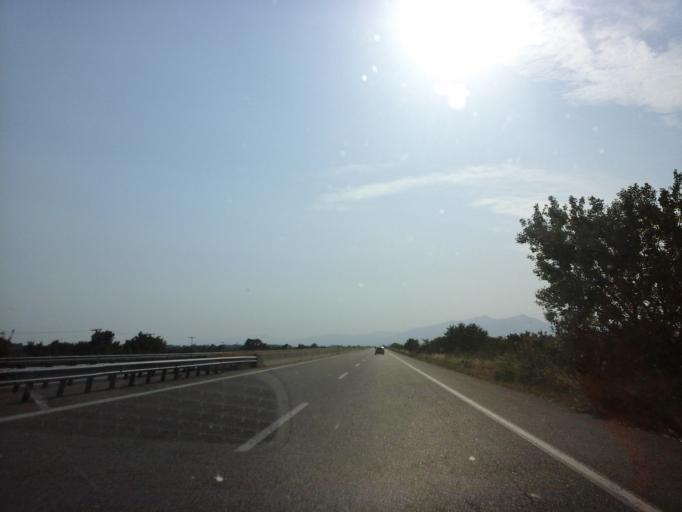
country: GR
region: East Macedonia and Thrace
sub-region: Nomos Xanthis
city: Selero
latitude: 41.1196
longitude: 25.0511
